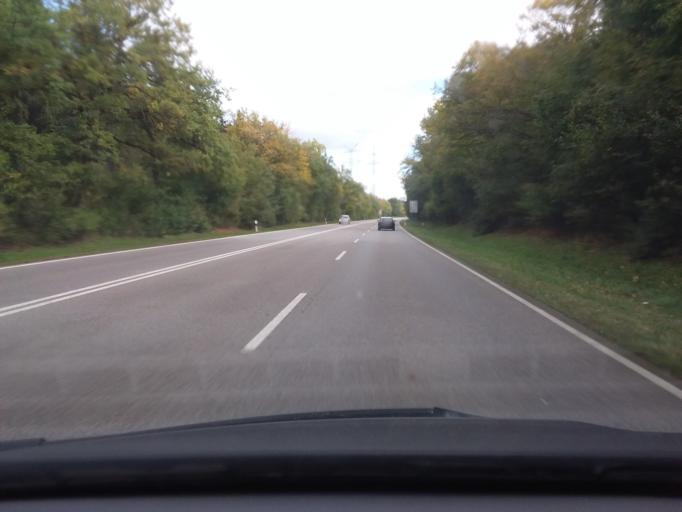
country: DE
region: Bavaria
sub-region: Upper Bavaria
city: Bergkirchen
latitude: 48.2389
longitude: 11.3872
